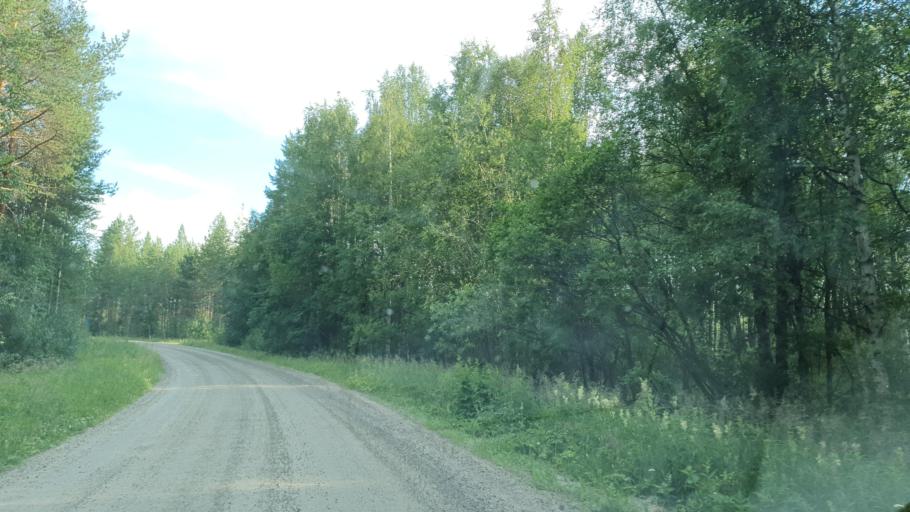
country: FI
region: Kainuu
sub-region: Kehys-Kainuu
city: Kuhmo
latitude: 64.2708
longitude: 29.8053
